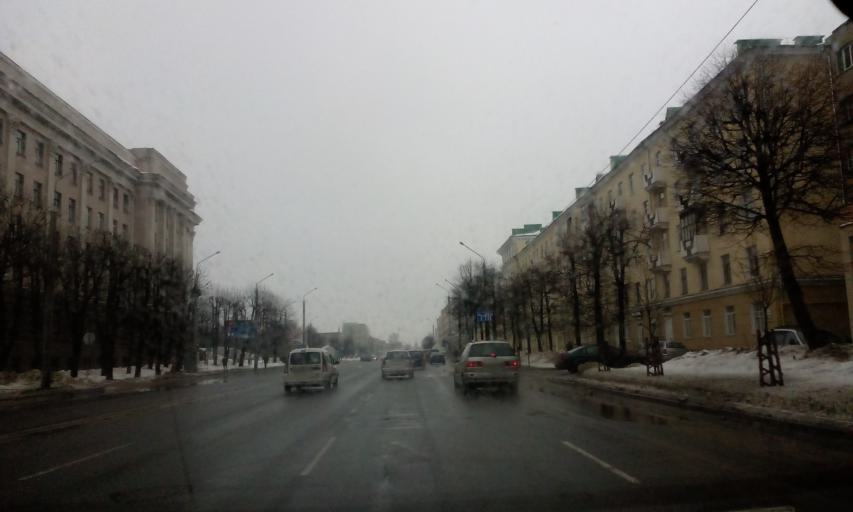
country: BY
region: Mogilev
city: Mahilyow
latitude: 53.9070
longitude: 30.3453
